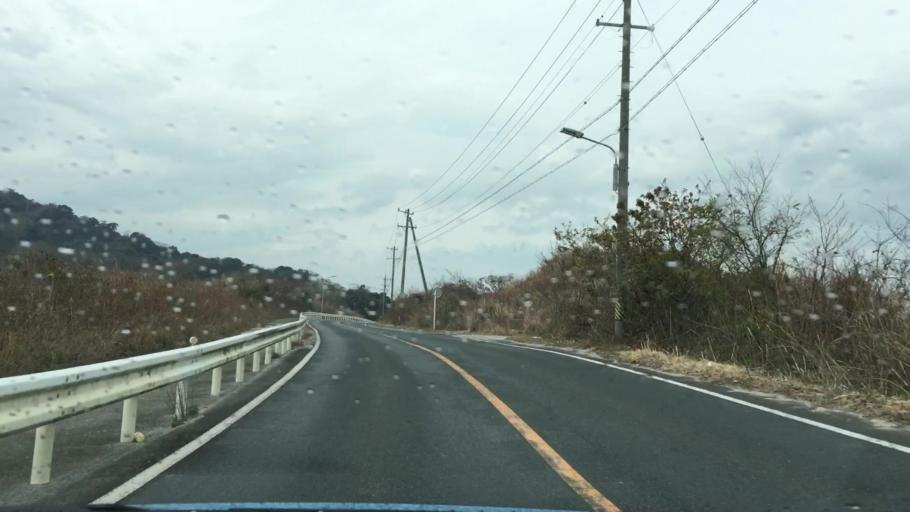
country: JP
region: Aichi
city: Tahara
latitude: 34.6834
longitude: 137.2502
